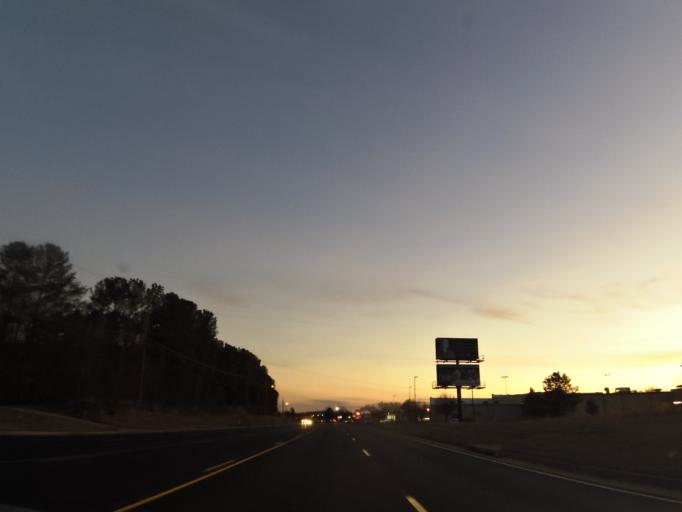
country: US
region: Georgia
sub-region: Whitfield County
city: Varnell
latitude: 34.8981
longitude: -84.9469
